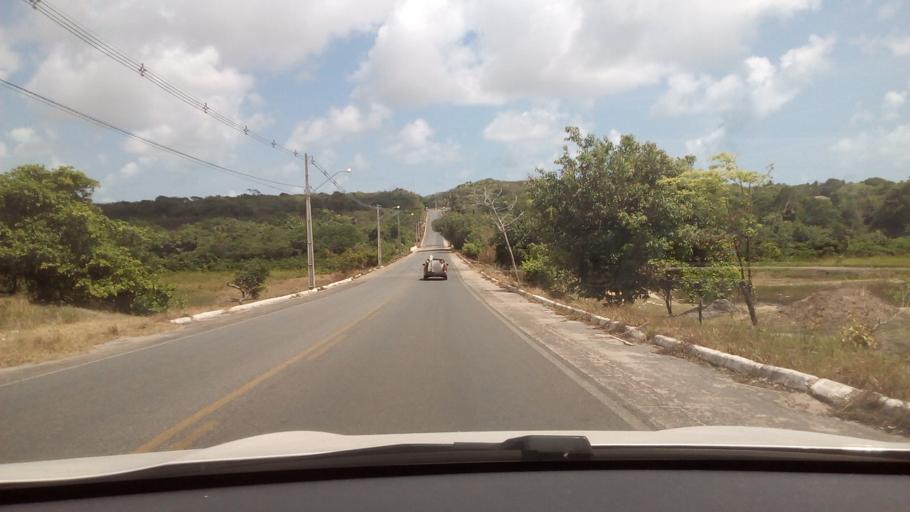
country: BR
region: Paraiba
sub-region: Joao Pessoa
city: Joao Pessoa
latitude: -7.2012
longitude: -34.8250
